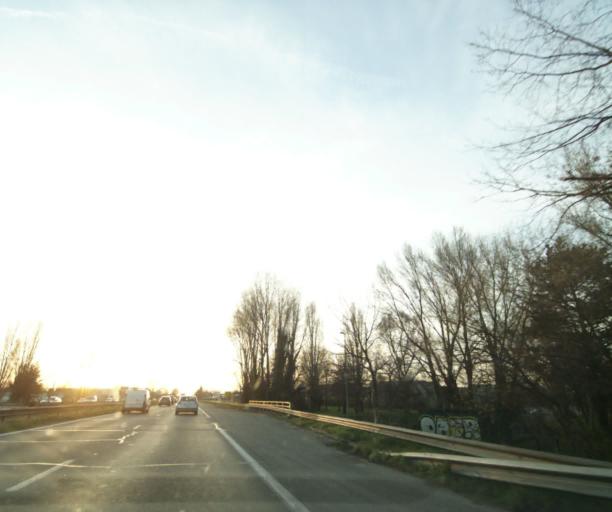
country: FR
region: Aquitaine
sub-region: Departement de la Gironde
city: Bruges
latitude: 44.8893
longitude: -0.5999
